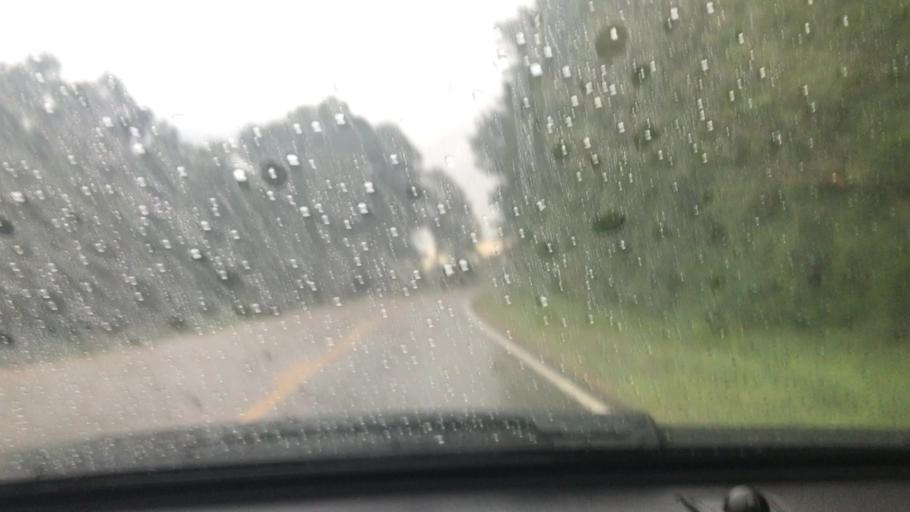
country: US
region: Mississippi
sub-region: Pike County
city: Summit
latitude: 31.3173
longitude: -90.5283
